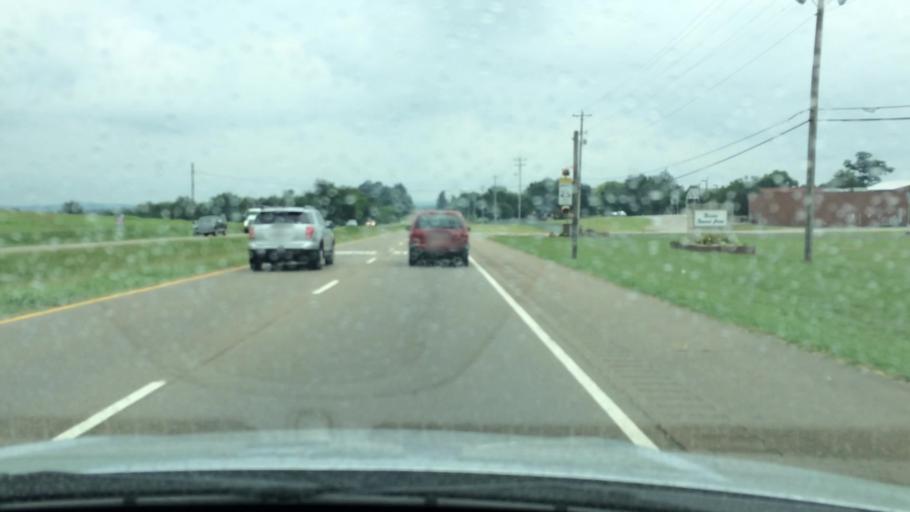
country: US
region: Tennessee
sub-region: Jefferson County
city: Jefferson City
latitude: 36.1098
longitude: -83.5152
